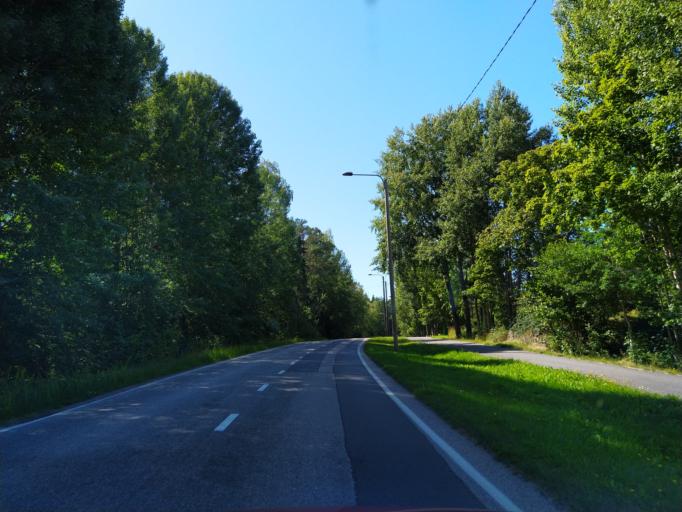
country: FI
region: Varsinais-Suomi
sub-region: Aboland-Turunmaa
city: Dragsfjaerd
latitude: 60.0197
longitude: 22.4937
